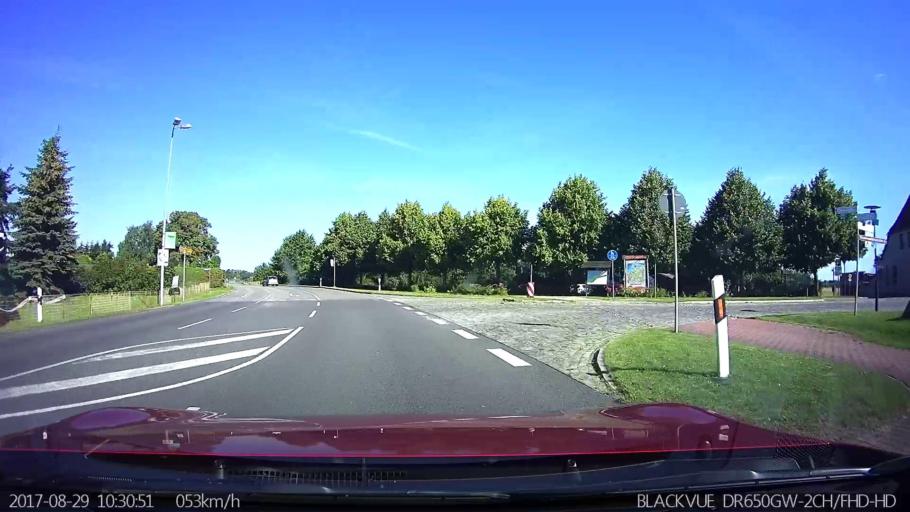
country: DE
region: Mecklenburg-Vorpommern
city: Tribsees
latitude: 54.0937
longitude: 12.7528
